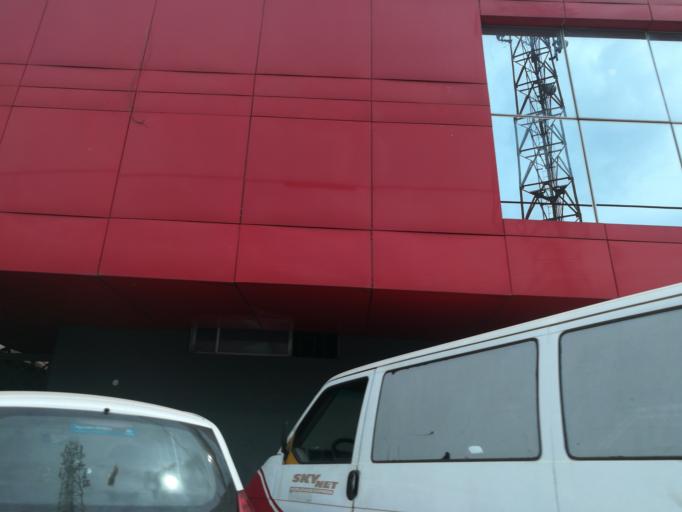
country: NG
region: Lagos
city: Ikeja
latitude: 6.5992
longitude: 3.3367
